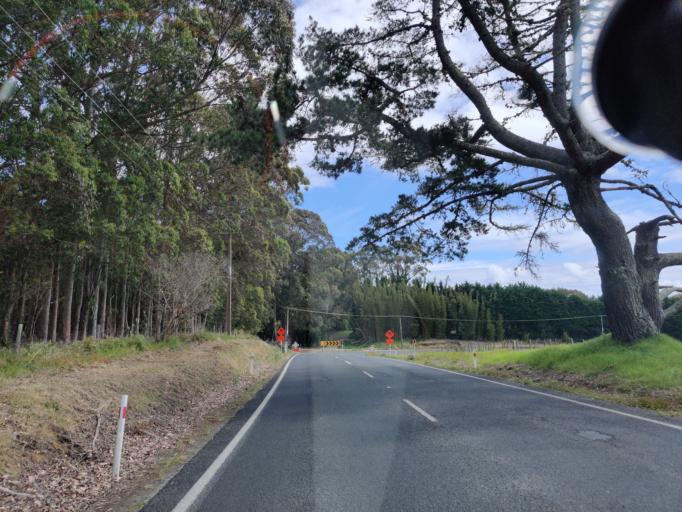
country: NZ
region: Northland
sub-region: Far North District
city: Kaitaia
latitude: -35.0026
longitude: 173.1914
